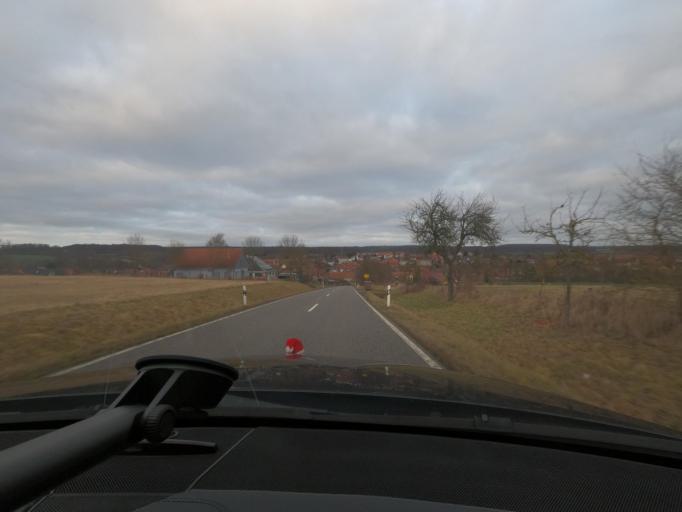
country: DE
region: Thuringia
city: Helmsdorf
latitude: 51.2749
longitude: 10.4041
